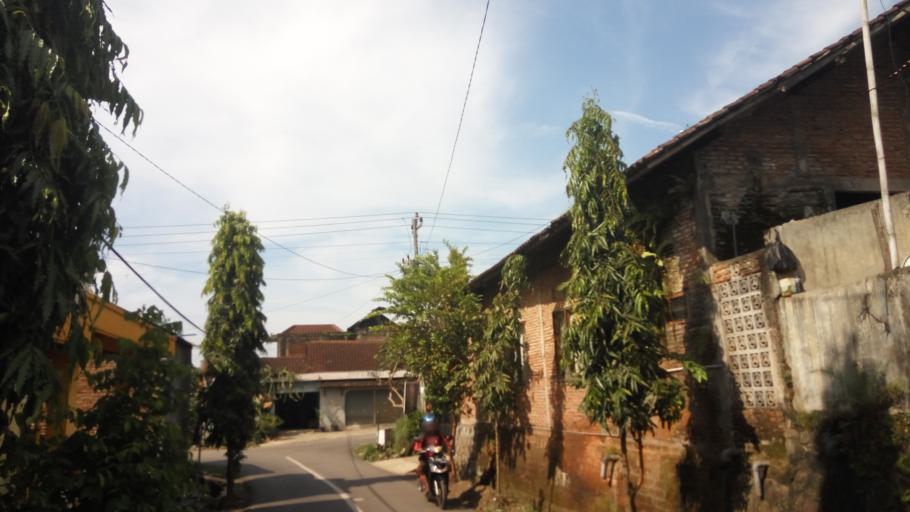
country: ID
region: Central Java
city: Ungaran
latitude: -7.1508
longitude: 110.4189
